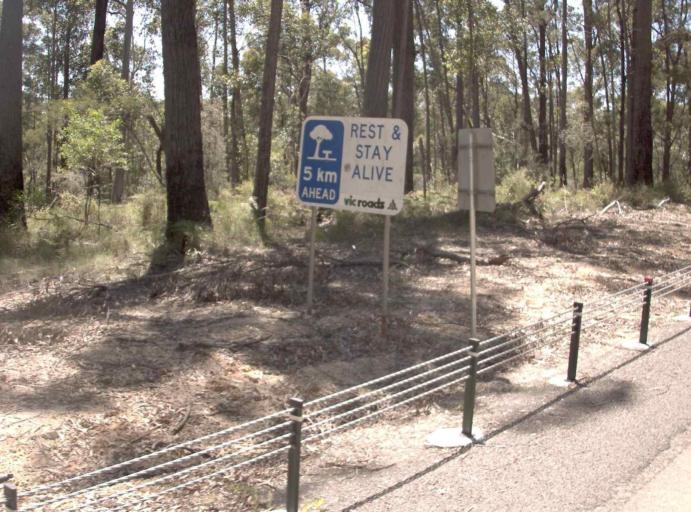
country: AU
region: Victoria
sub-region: East Gippsland
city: Lakes Entrance
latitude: -37.7044
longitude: 148.5772
